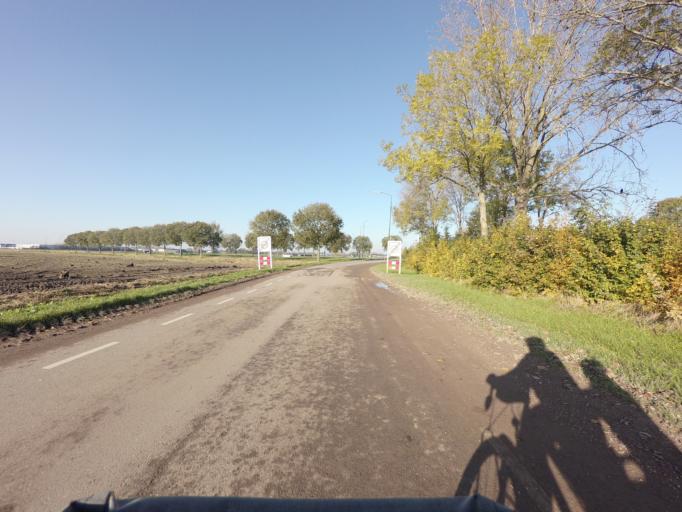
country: NL
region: North Brabant
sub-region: Gemeente Woudrichem
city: Woudrichem
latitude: 51.7726
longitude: 5.0492
